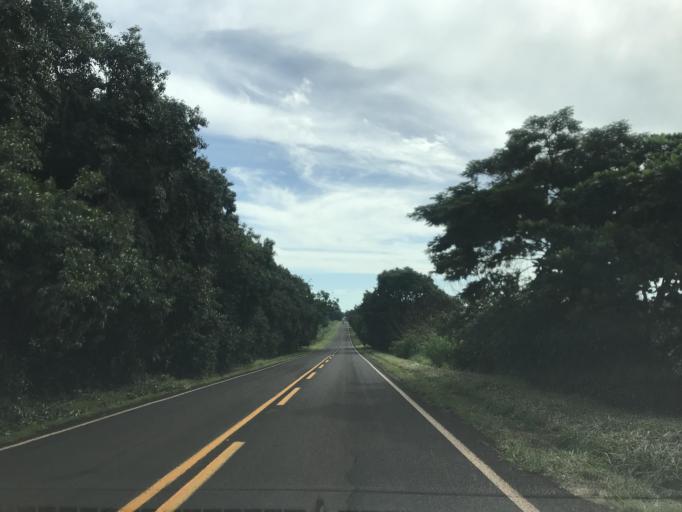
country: BR
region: Parana
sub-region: Terra Rica
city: Terra Rica
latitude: -22.7687
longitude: -52.6429
